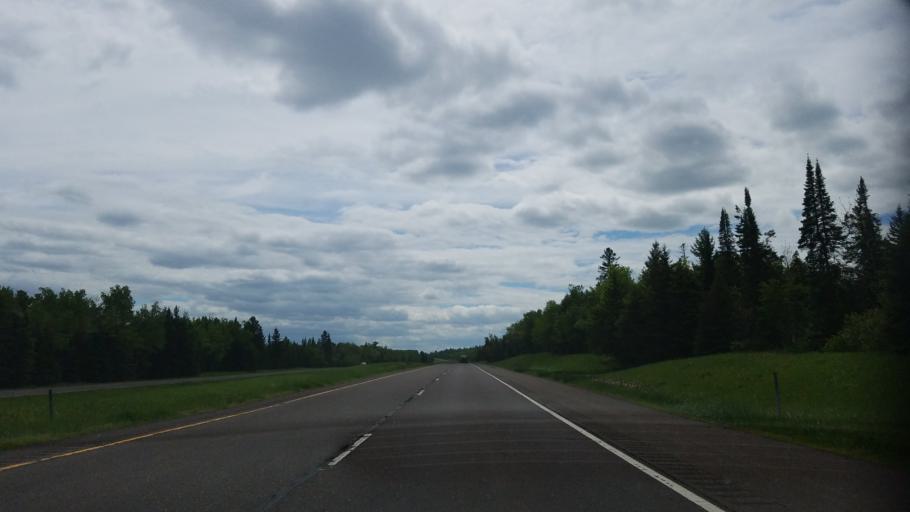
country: US
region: Minnesota
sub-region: Lake County
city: Two Harbors
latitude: 47.0051
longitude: -91.7186
